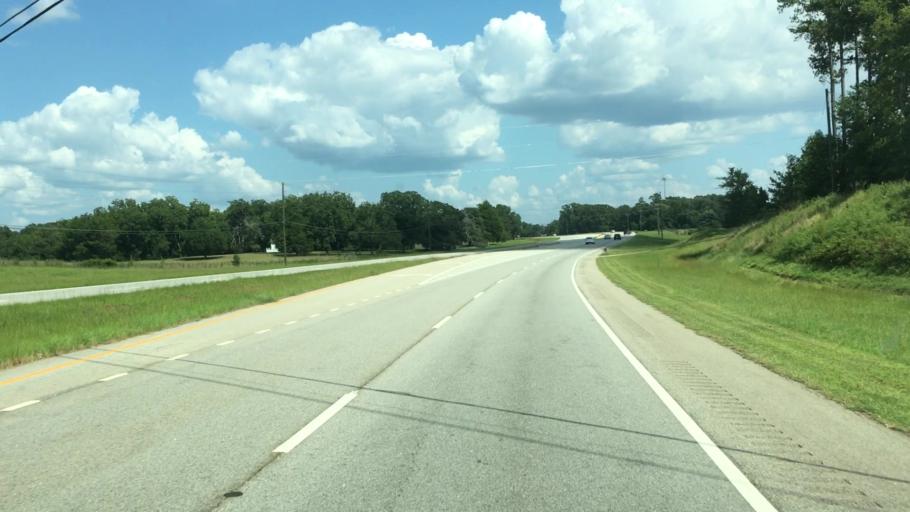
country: US
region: Georgia
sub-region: Putnam County
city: Eatonton
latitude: 33.2720
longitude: -83.3475
